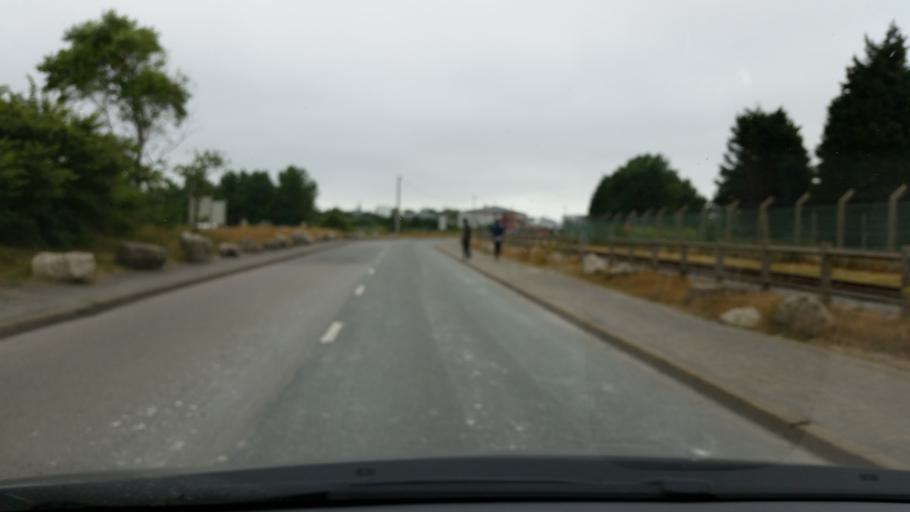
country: FR
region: Nord-Pas-de-Calais
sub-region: Departement du Pas-de-Calais
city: Calais
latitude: 50.9642
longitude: 1.8774
